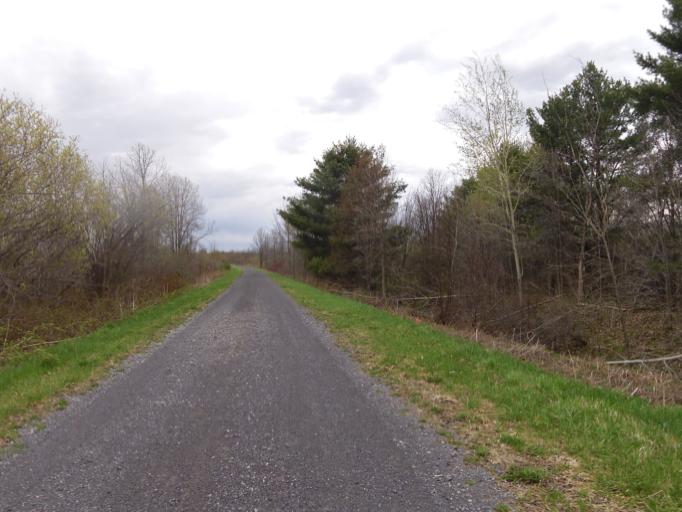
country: CA
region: Quebec
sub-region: Outaouais
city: Papineauville
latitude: 45.5193
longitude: -74.9727
